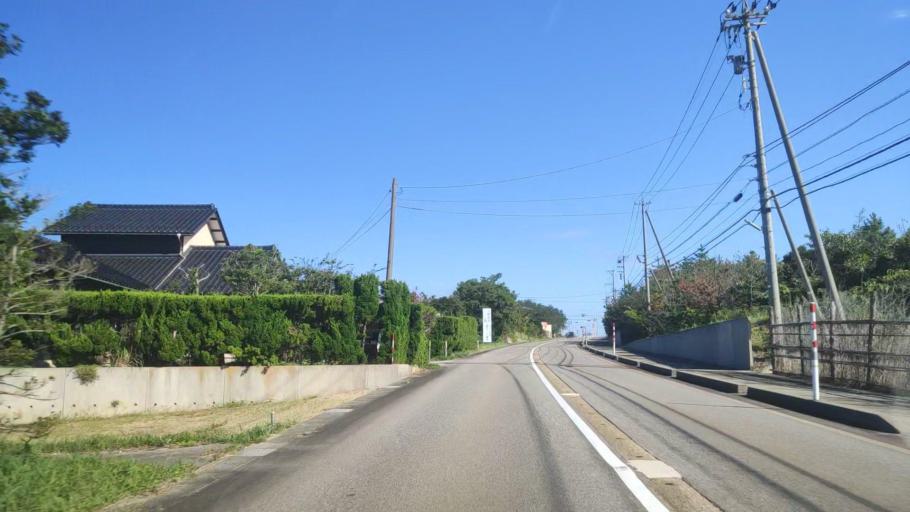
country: JP
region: Ishikawa
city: Hakui
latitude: 36.9858
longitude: 136.7757
